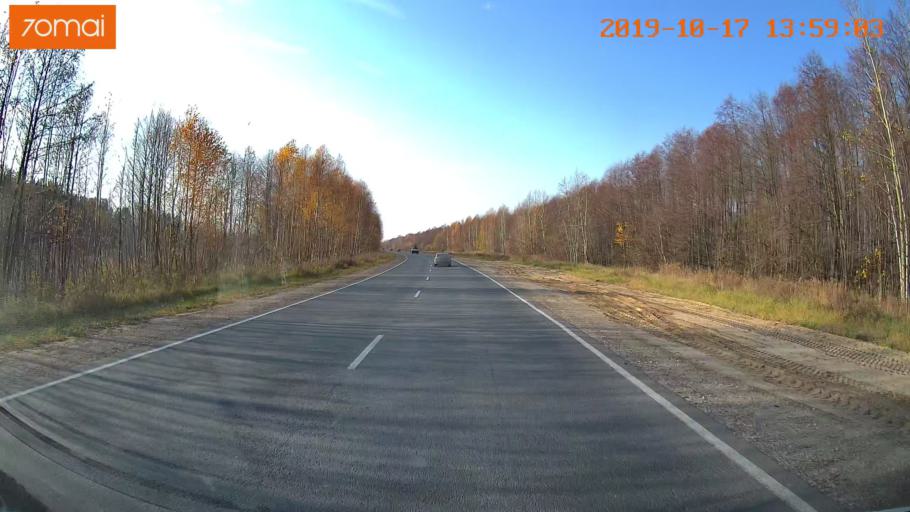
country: RU
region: Rjazan
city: Spas-Klepiki
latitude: 55.1412
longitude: 40.2122
